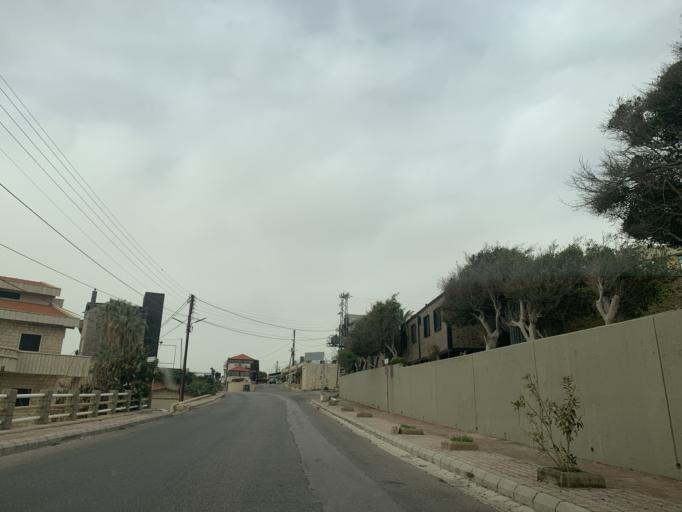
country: LB
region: Mont-Liban
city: Jbail
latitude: 34.0827
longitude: 35.6489
